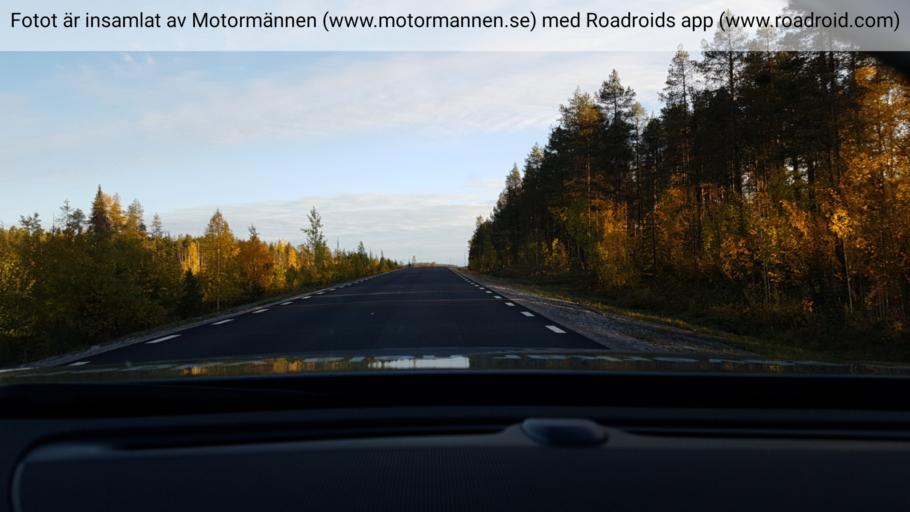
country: SE
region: Norrbotten
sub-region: Jokkmokks Kommun
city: Jokkmokk
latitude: 66.5845
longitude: 19.8042
